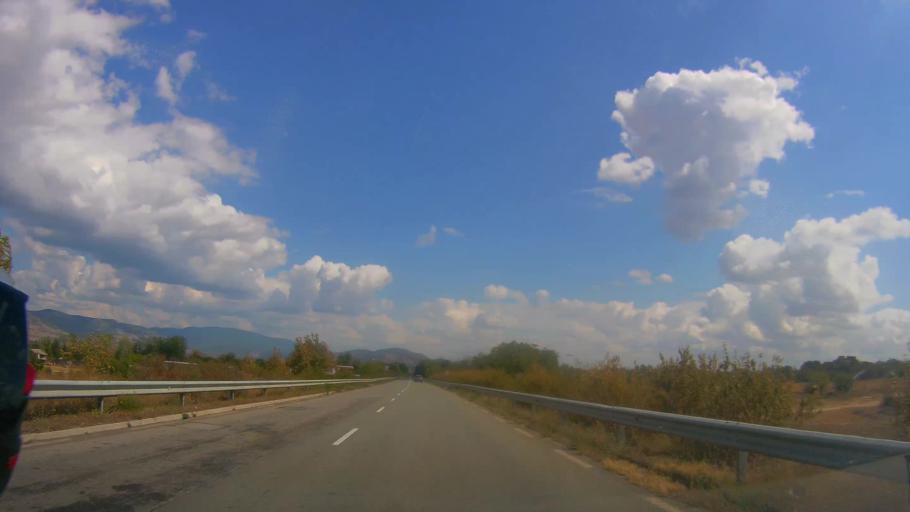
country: BG
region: Sliven
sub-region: Obshtina Tvurditsa
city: Tvurditsa
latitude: 42.6541
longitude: 25.9475
